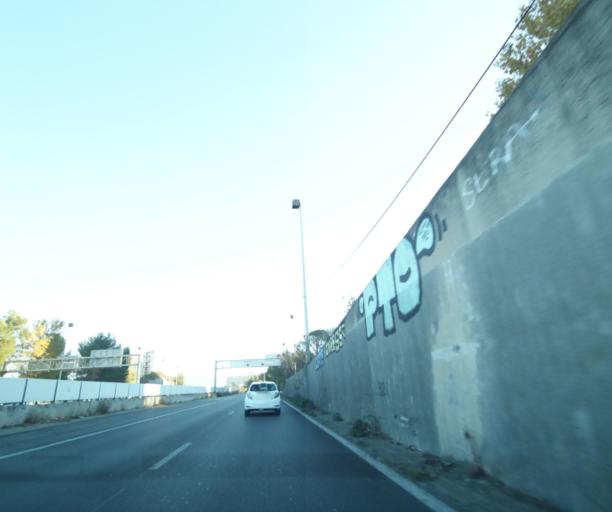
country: FR
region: Provence-Alpes-Cote d'Azur
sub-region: Departement des Bouches-du-Rhone
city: Marseille 13
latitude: 43.3167
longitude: 5.4110
